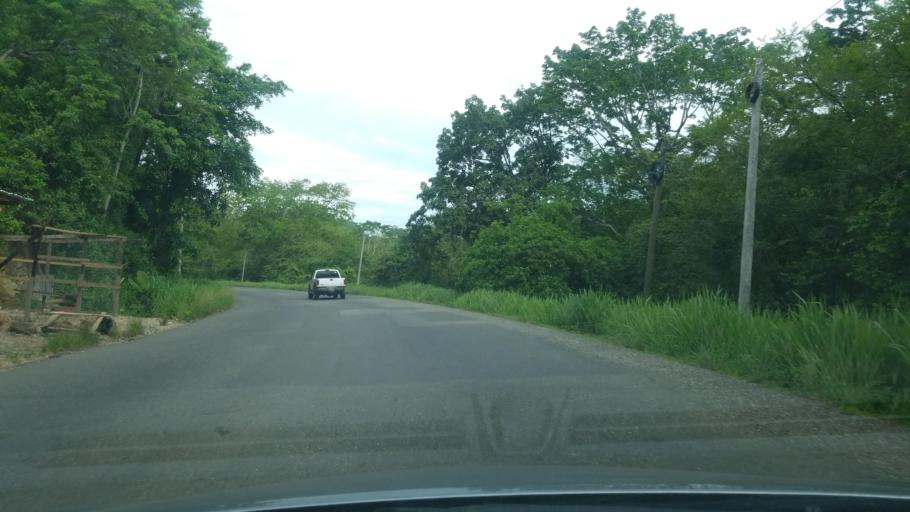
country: HN
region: Santa Barbara
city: Camalote
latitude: 15.3317
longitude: -88.2973
